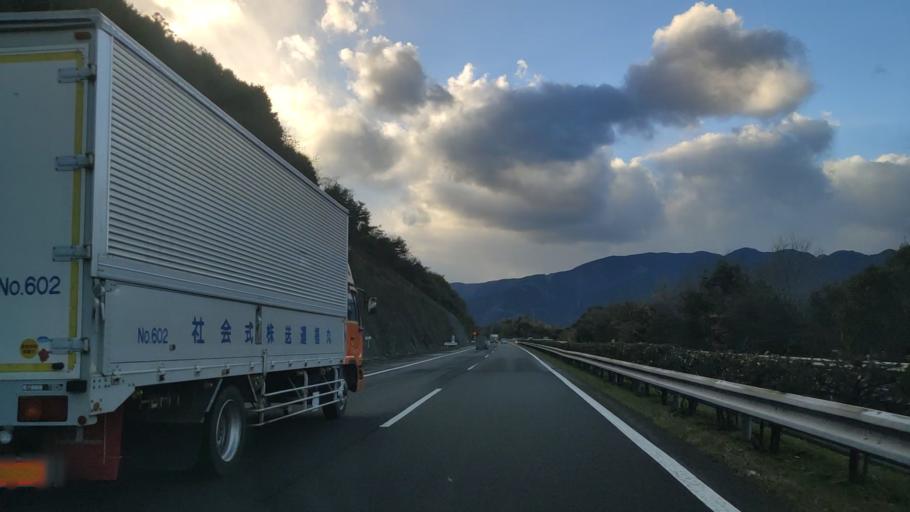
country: JP
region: Ehime
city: Saijo
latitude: 33.8558
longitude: 133.0283
